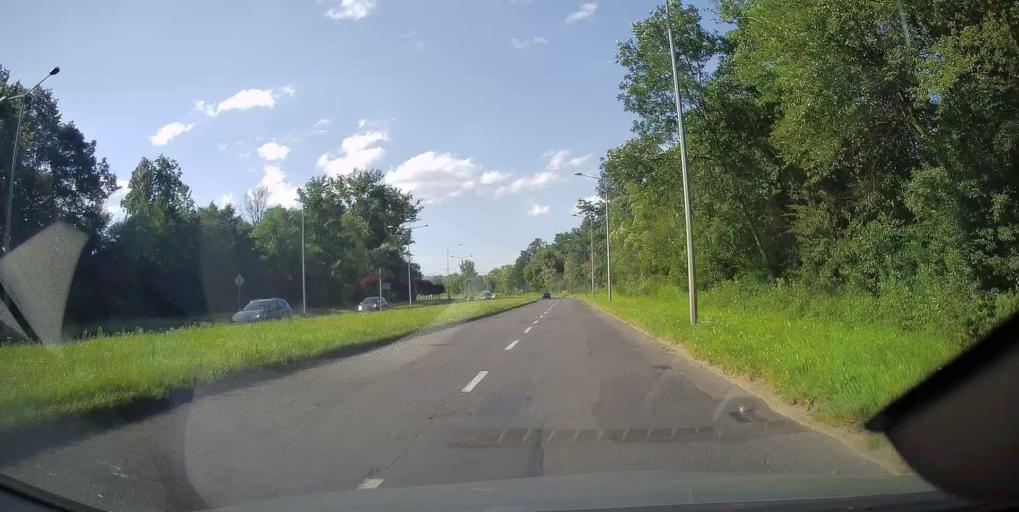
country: PL
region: Lesser Poland Voivodeship
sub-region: Powiat nowosadecki
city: Nowy Sacz
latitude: 49.6065
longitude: 20.7287
